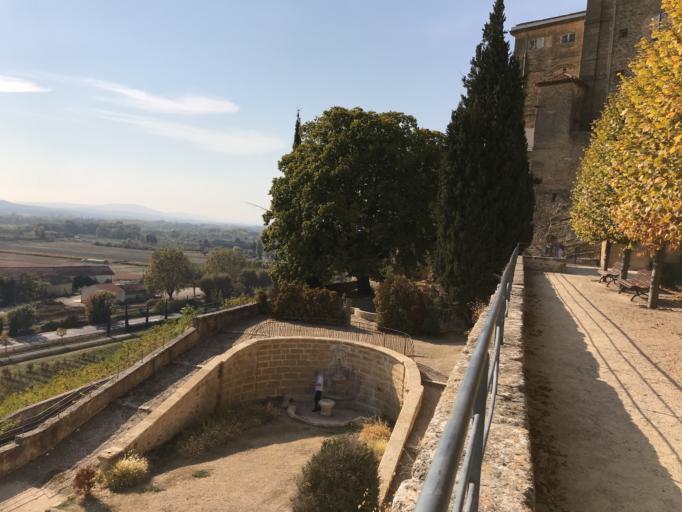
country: FR
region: Provence-Alpes-Cote d'Azur
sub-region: Departement du Vaucluse
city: Lauris
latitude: 43.7458
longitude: 5.3114
